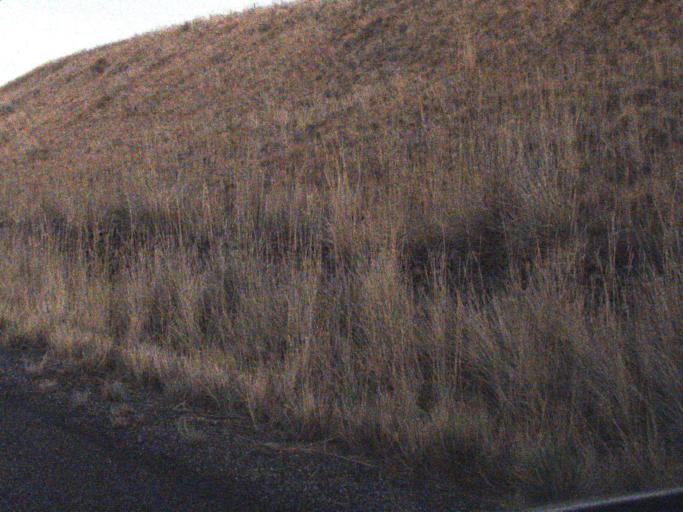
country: US
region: Washington
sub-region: Garfield County
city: Pomeroy
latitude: 46.5259
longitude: -117.7927
